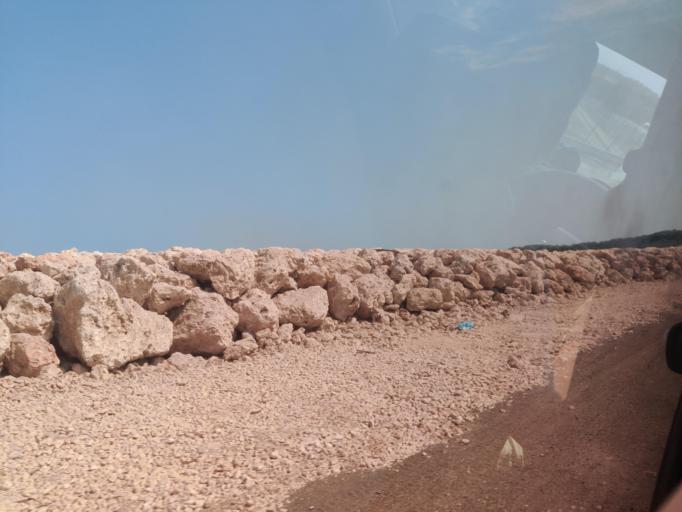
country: CO
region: Bolivar
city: Turbana
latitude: 10.1899
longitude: -75.6362
